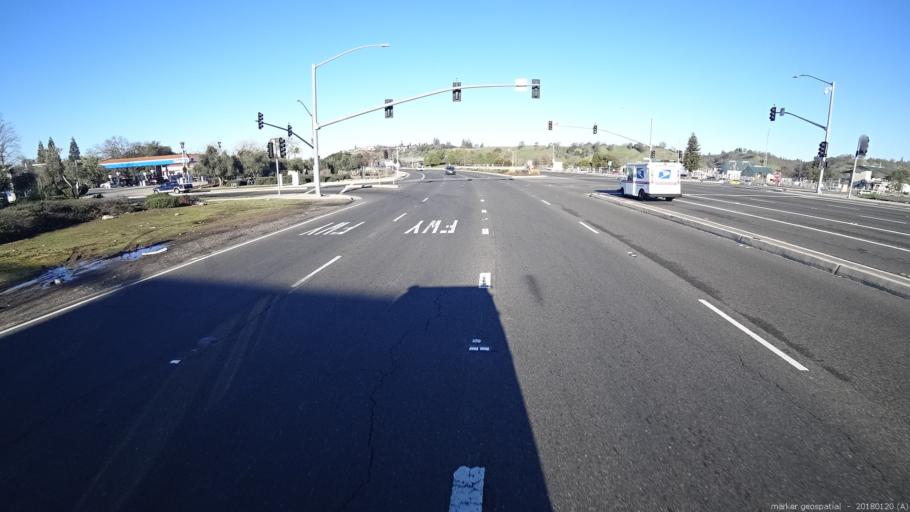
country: US
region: California
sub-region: Sacramento County
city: Gold River
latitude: 38.6325
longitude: -121.2187
